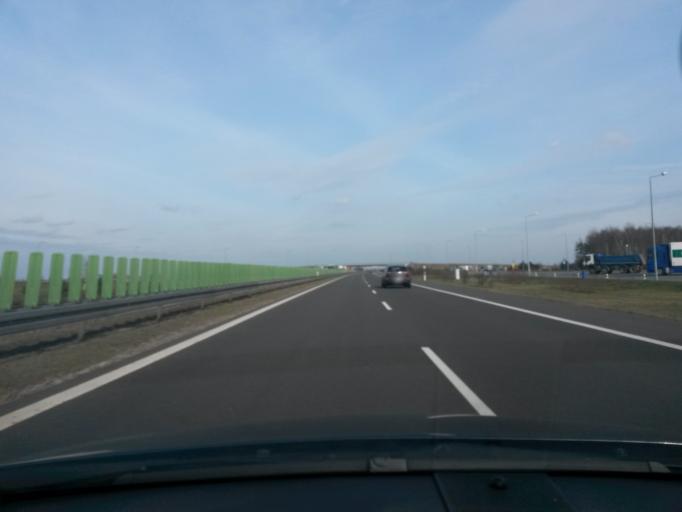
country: PL
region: Greater Poland Voivodeship
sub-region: Powiat wrzesinski
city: Nekla
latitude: 52.3180
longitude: 17.4196
